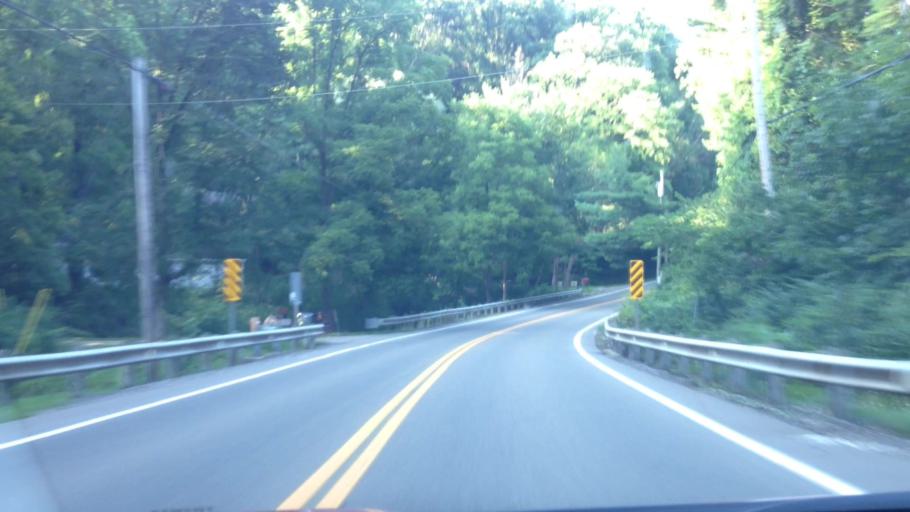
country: US
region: Ohio
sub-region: Summit County
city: Fairlawn
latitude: 41.1588
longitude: -81.6080
